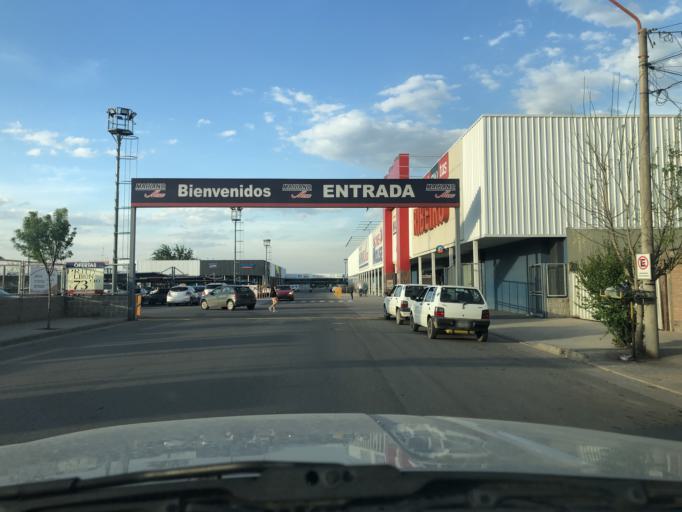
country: AR
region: Cordoba
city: Jesus Maria
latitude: -30.9773
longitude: -64.0836
